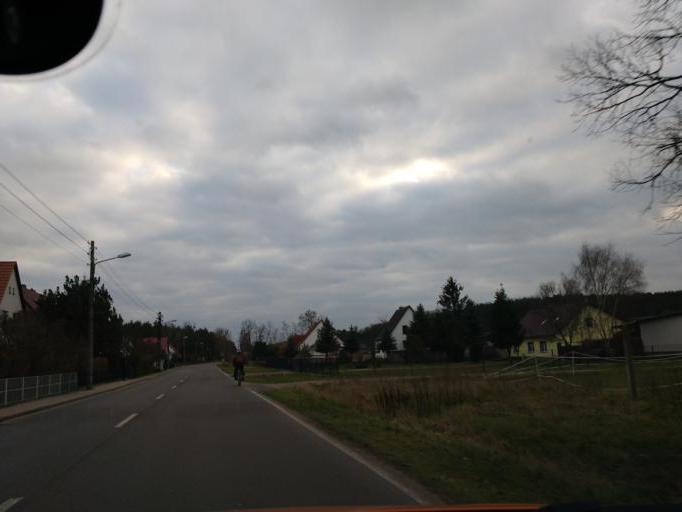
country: DE
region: Brandenburg
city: Wriezen
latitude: 52.7015
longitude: 14.1348
